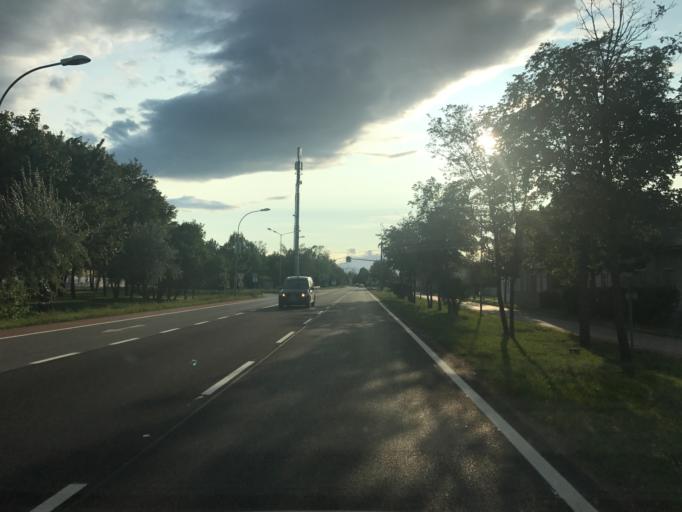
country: AT
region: Lower Austria
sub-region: Wiener Neustadt Stadt
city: Wiener Neustadt
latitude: 47.8086
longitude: 16.2282
